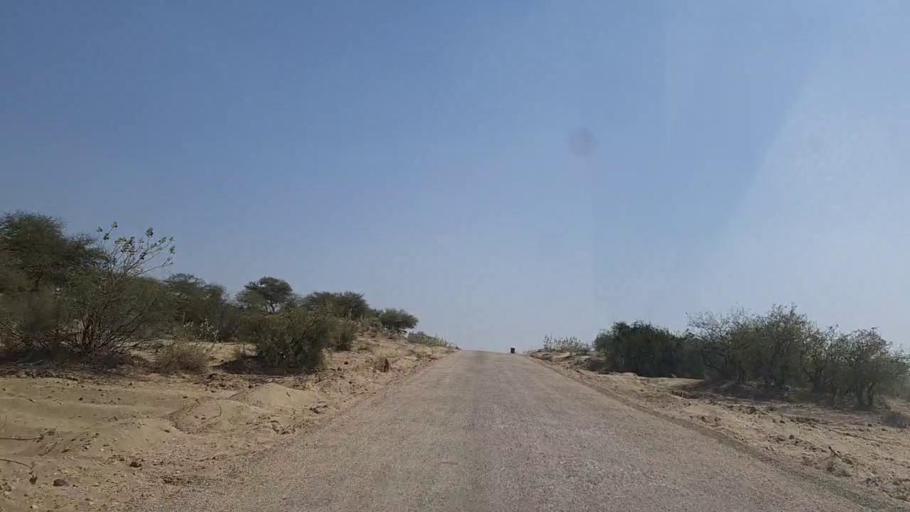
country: PK
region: Sindh
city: Diplo
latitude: 24.4801
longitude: 69.4978
